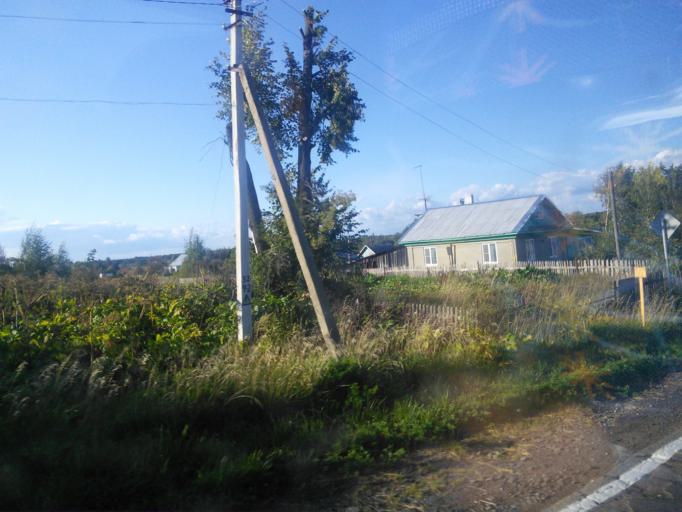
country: RU
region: Jaroslavl
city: Poshekhon'ye
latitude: 58.4251
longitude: 38.9956
